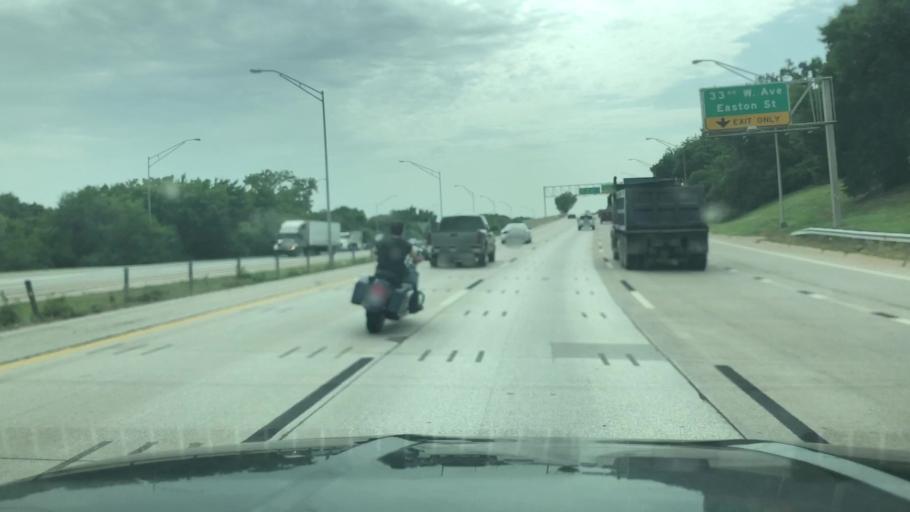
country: US
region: Oklahoma
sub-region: Tulsa County
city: Tulsa
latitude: 36.1566
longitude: -96.0248
